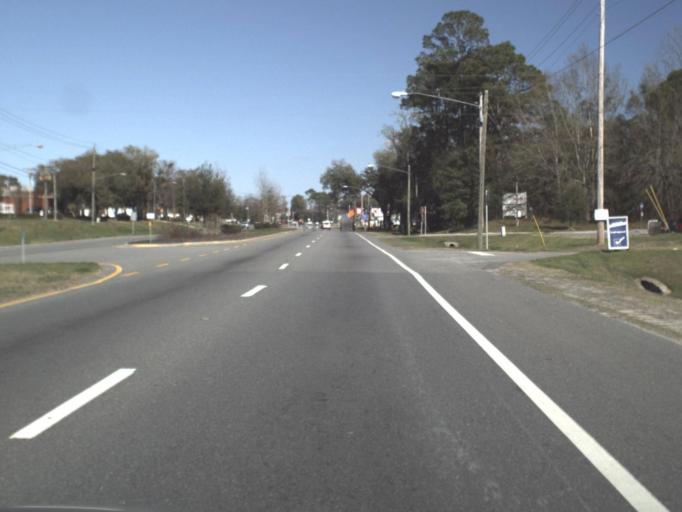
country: US
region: Florida
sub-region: Leon County
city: Tallahassee
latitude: 30.4572
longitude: -84.3659
